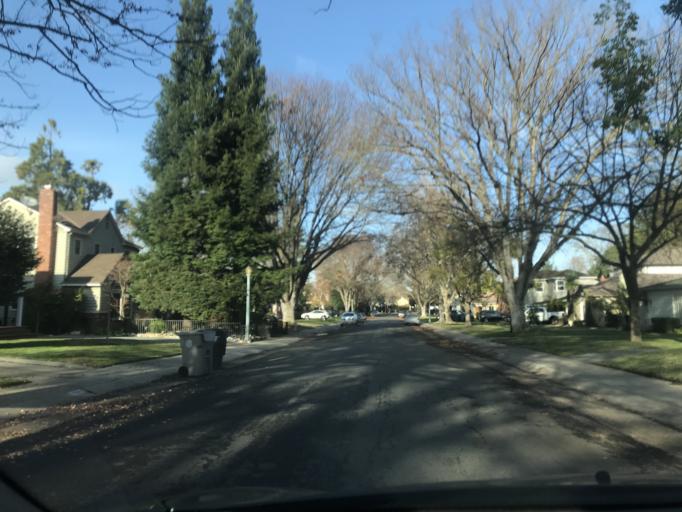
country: US
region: California
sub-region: Sacramento County
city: Sacramento
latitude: 38.5592
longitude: -121.4964
